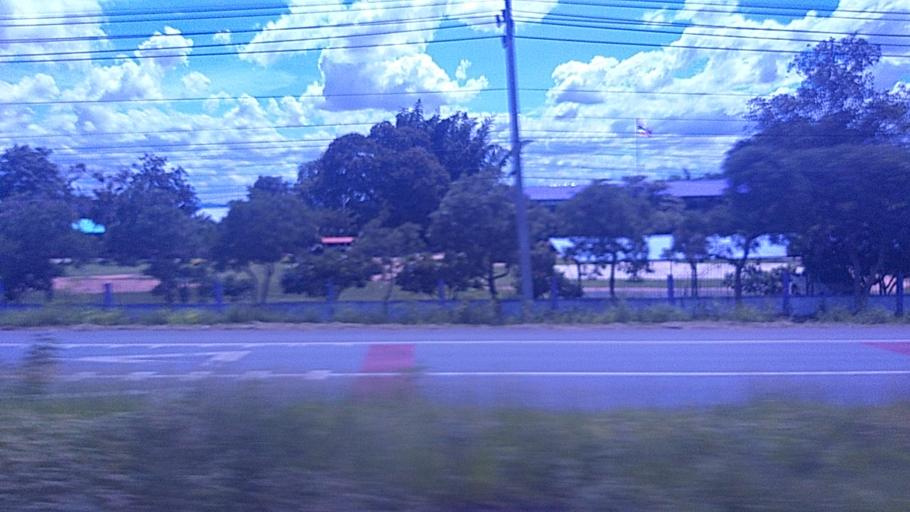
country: TH
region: Nakhon Ratchasima
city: Dan Khun Thot
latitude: 15.0960
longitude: 101.7208
